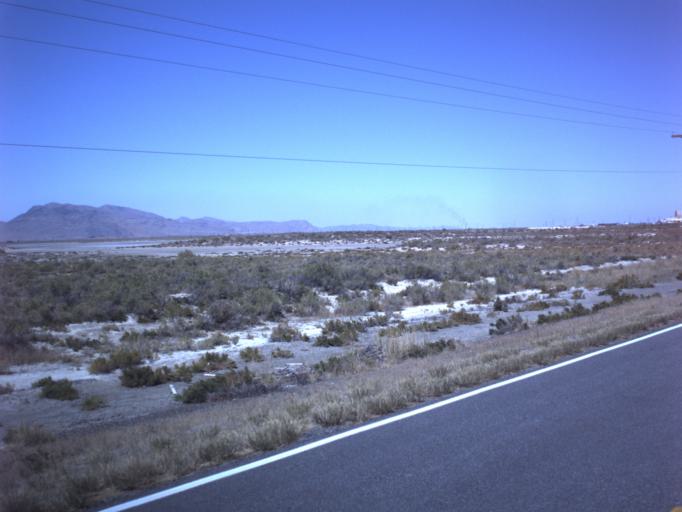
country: US
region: Utah
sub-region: Tooele County
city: Grantsville
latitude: 40.7322
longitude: -112.6570
